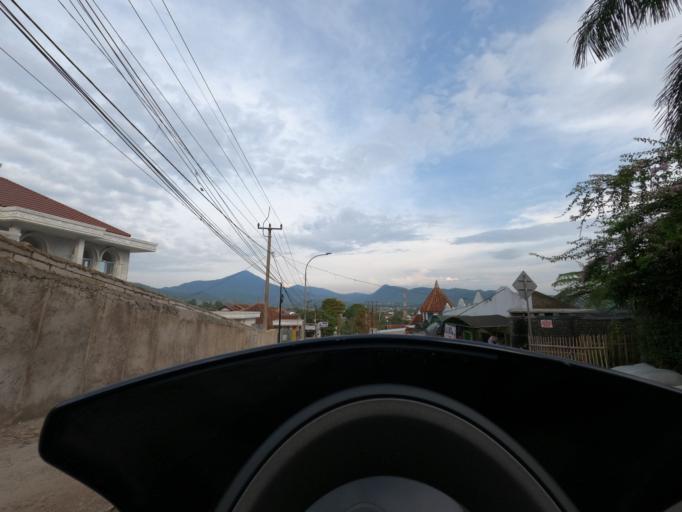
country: ID
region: West Java
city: Lembang
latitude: -6.8075
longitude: 107.6395
